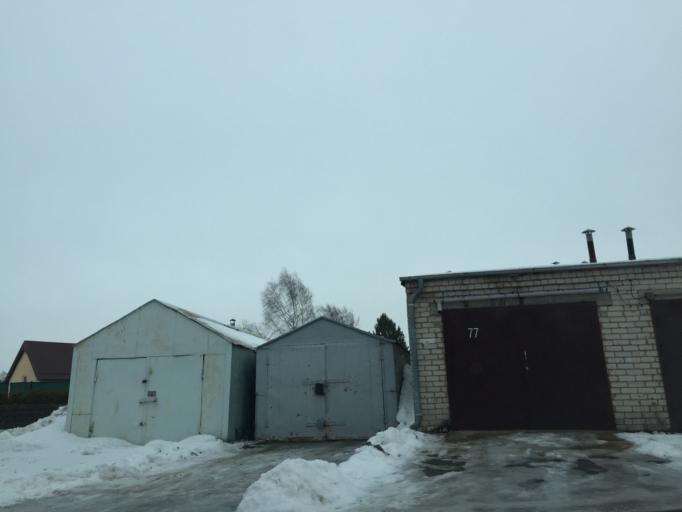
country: LV
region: Ikskile
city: Ikskile
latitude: 56.8453
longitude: 24.4415
